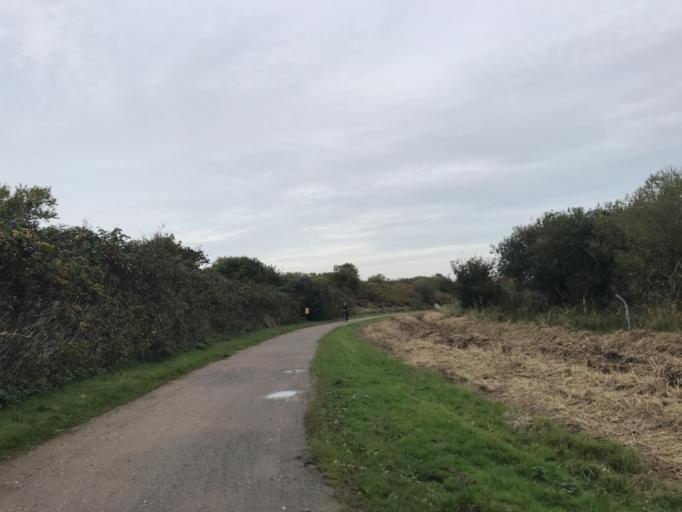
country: DE
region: Lower Saxony
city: Borkum
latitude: 53.5996
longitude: 6.7025
